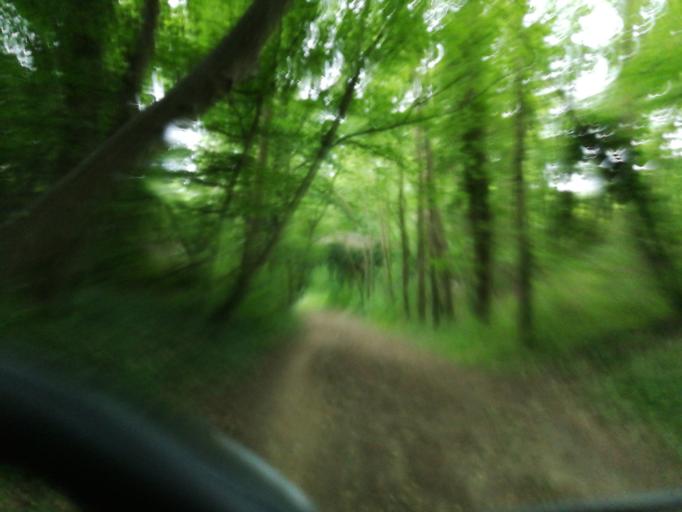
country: FR
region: Ile-de-France
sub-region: Departement des Yvelines
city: Saint-Remy-les-Chevreuse
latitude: 48.6986
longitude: 2.0604
